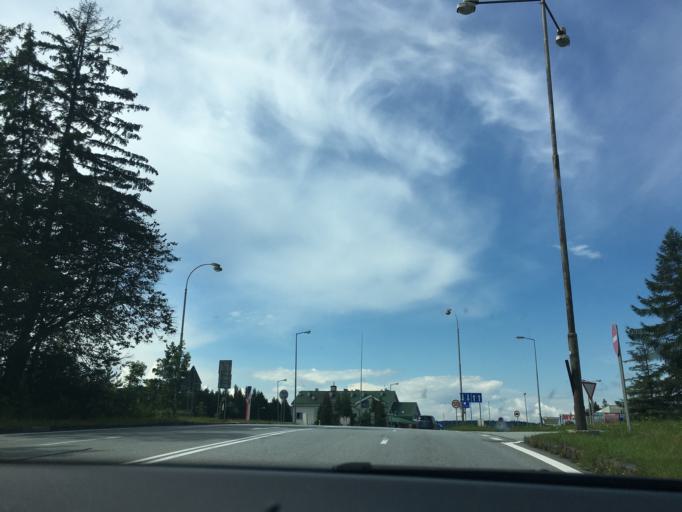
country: PL
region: Subcarpathian Voivodeship
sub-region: Powiat krosnienski
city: Jasliska
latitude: 49.4171
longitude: 21.6969
